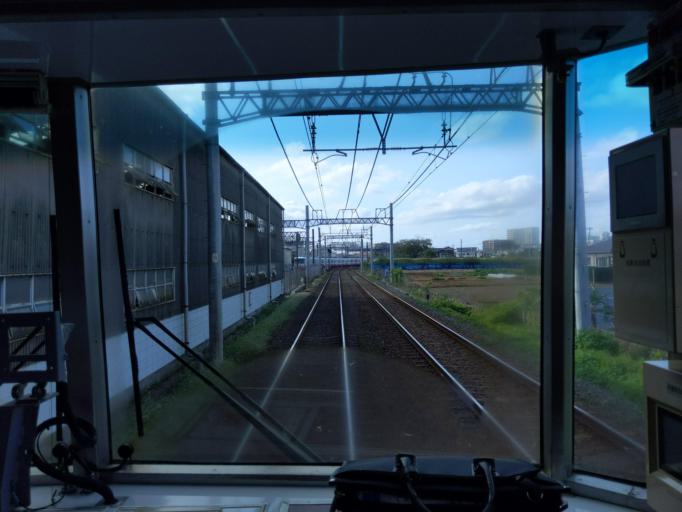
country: JP
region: Chiba
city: Kashiwa
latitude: 35.7786
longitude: 139.9783
